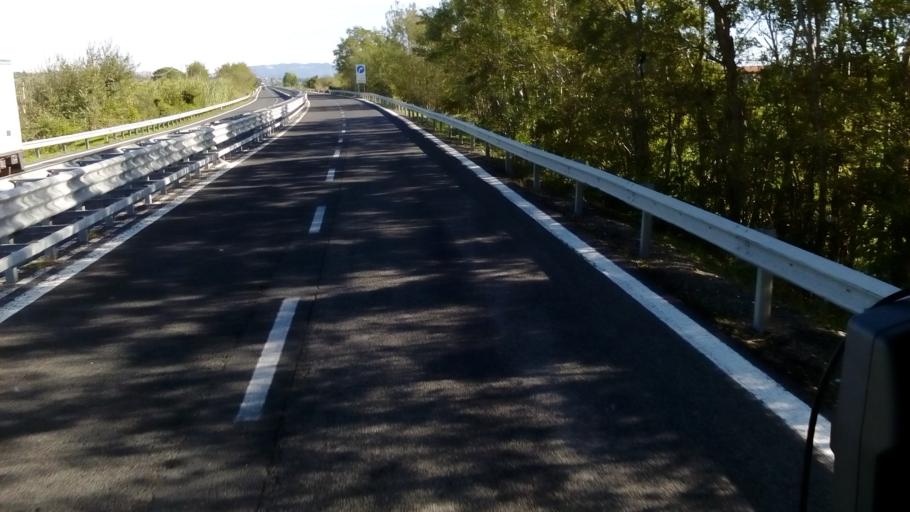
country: IT
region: Latium
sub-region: Provincia di Viterbo
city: Tarquinia
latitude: 42.2823
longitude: 11.6932
